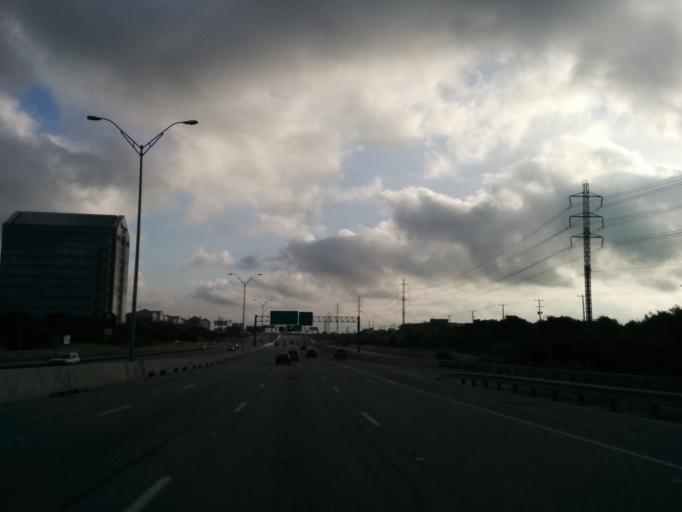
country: US
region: Texas
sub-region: Bexar County
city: Alamo Heights
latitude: 29.5022
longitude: -98.4809
